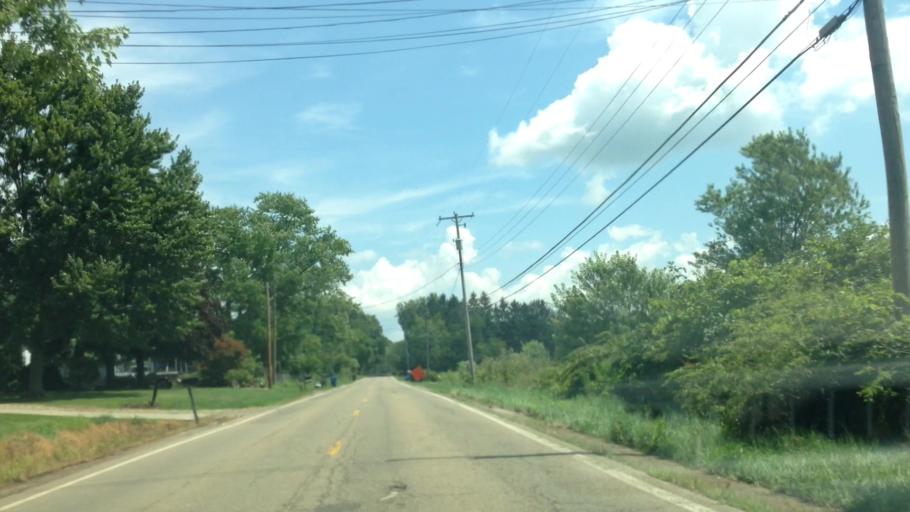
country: US
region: Ohio
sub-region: Summit County
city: Clinton
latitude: 40.9497
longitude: -81.6062
